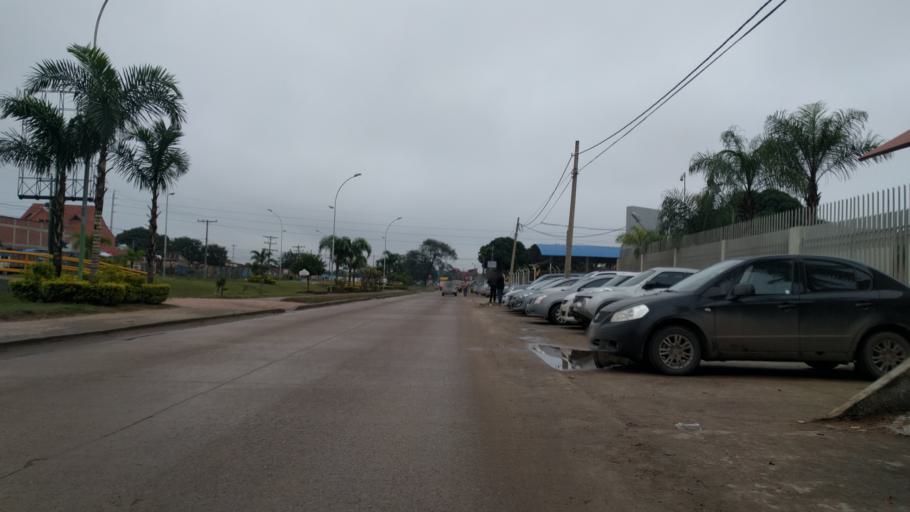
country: BO
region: Santa Cruz
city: Santa Cruz de la Sierra
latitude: -17.8182
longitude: -63.2116
